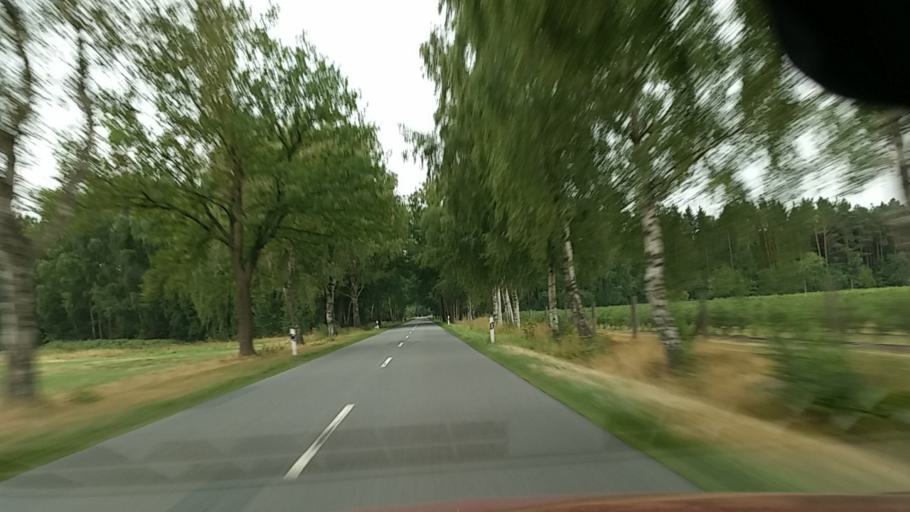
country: DE
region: Lower Saxony
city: Schoneworde
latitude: 52.6496
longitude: 10.6989
